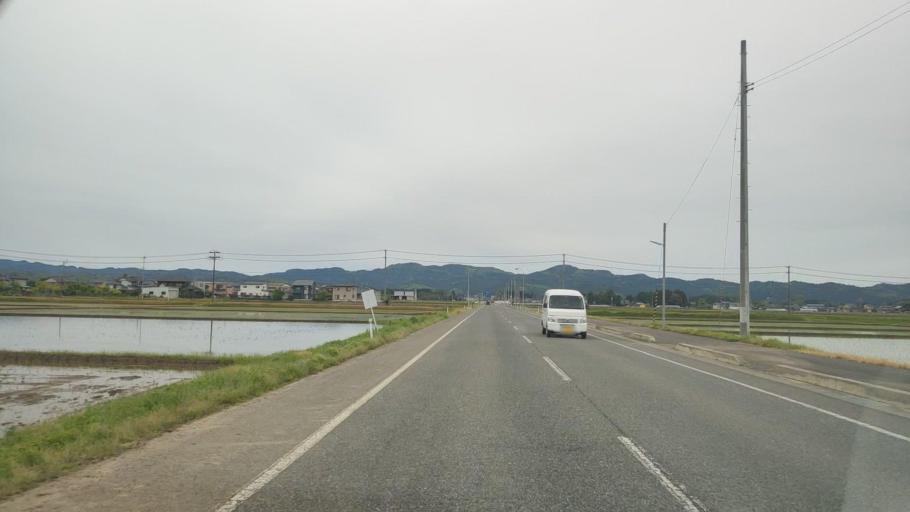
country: JP
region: Niigata
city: Gosen
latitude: 37.7292
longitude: 139.1723
